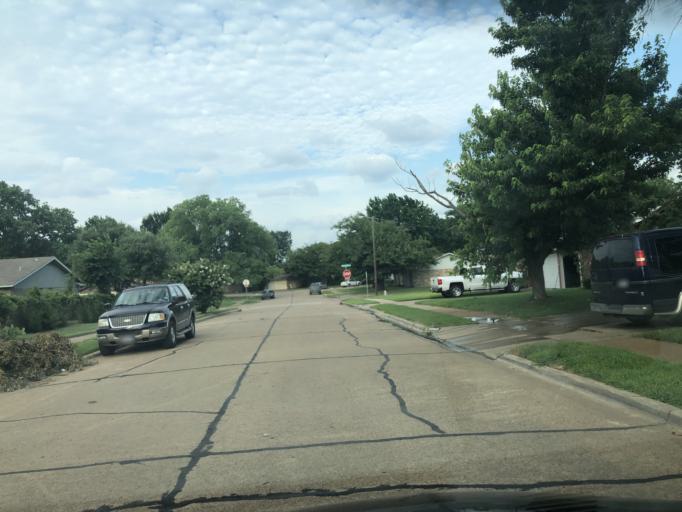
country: US
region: Texas
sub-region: Dallas County
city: Irving
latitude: 32.7883
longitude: -96.9703
